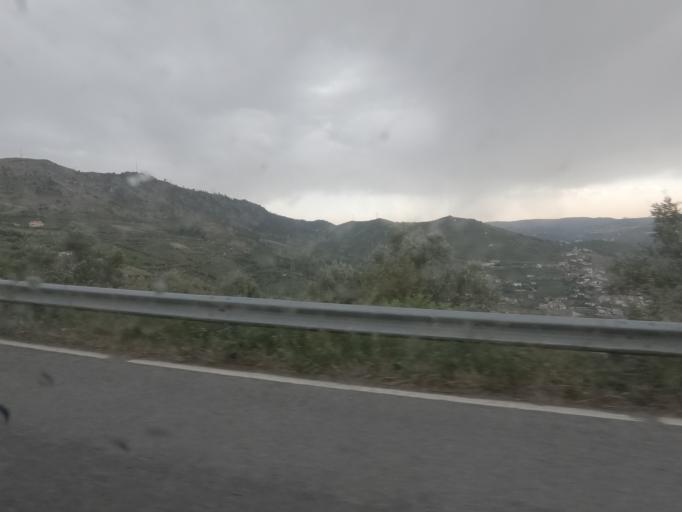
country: PT
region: Vila Real
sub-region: Peso da Regua
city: Peso da Regua
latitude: 41.1348
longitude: -7.7549
